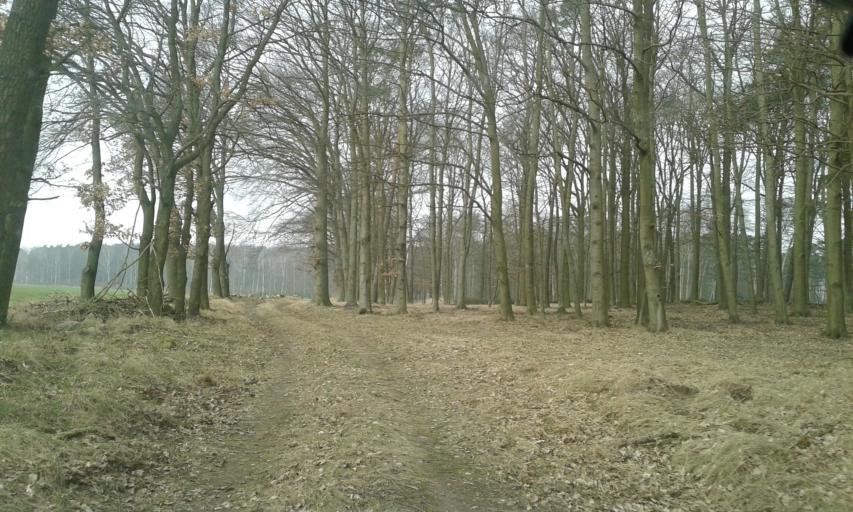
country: PL
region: West Pomeranian Voivodeship
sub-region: Powiat choszczenski
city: Pelczyce
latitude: 53.0806
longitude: 15.2569
